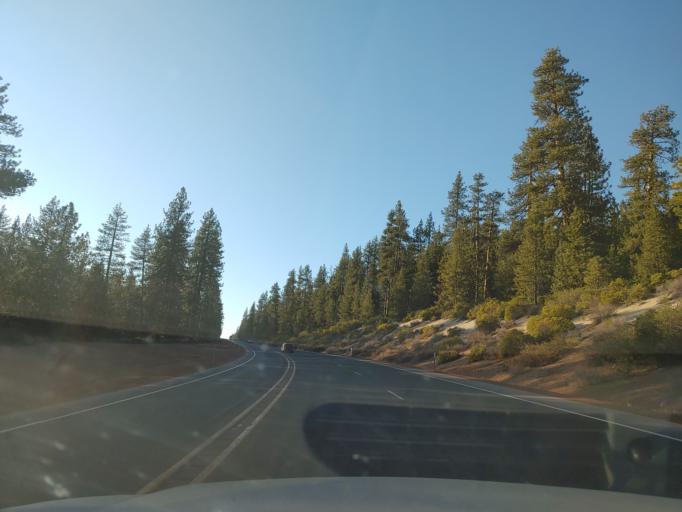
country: US
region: Oregon
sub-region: Deschutes County
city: La Pine
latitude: 43.4505
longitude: -121.8698
